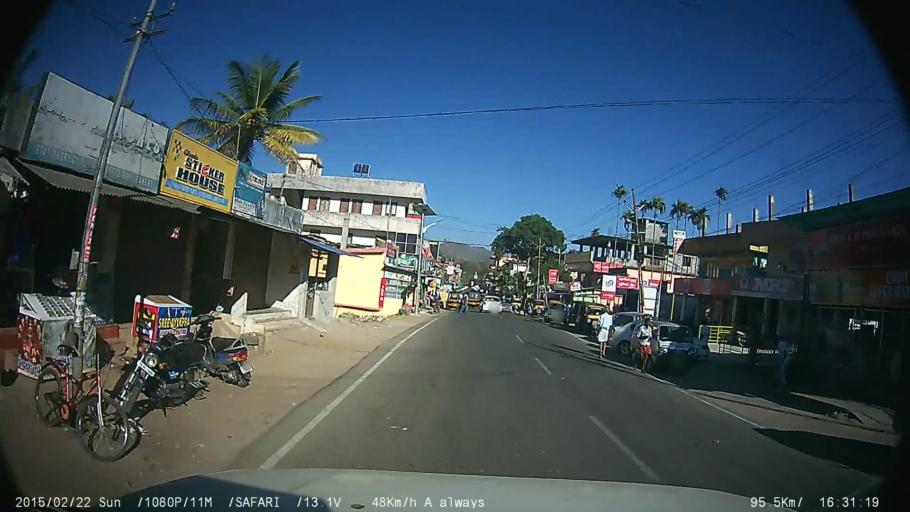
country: IN
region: Tamil Nadu
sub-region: Theni
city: Gudalur
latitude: 9.6067
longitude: 77.1635
